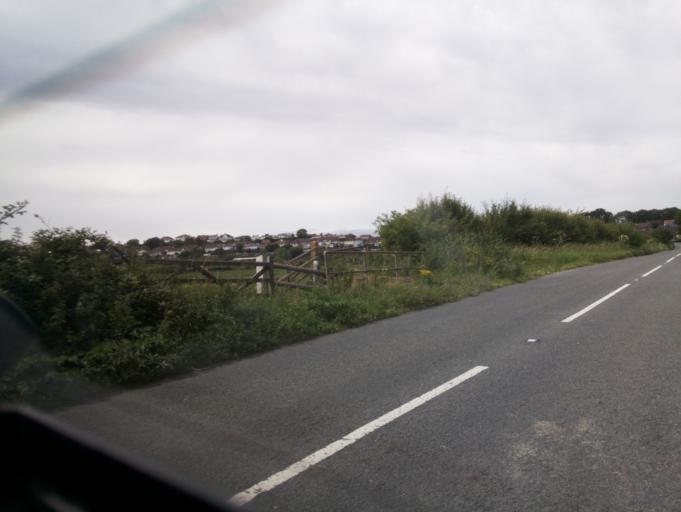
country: GB
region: England
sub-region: Somerset
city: Glastonbury
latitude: 51.1392
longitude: -2.7132
